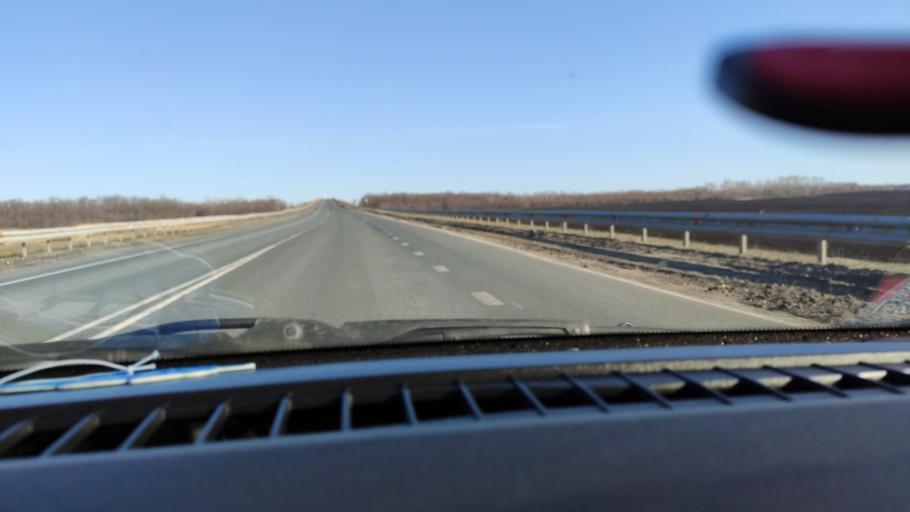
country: RU
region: Saratov
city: Dukhovnitskoye
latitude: 52.7470
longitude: 48.2508
